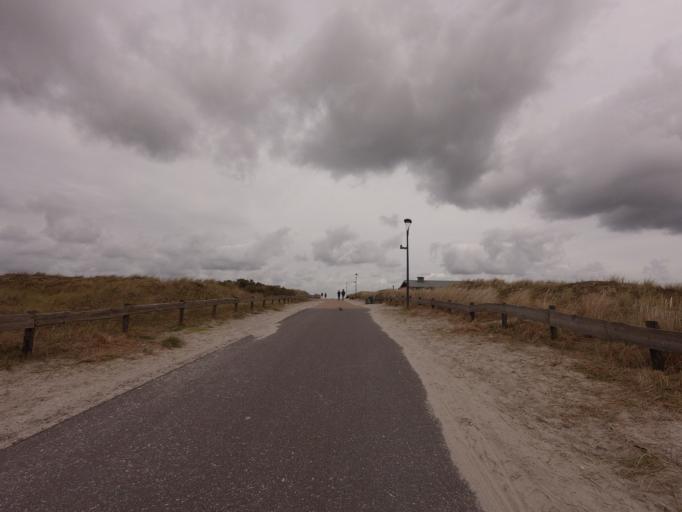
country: NL
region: Friesland
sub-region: Gemeente Ameland
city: Hollum
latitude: 53.4585
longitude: 5.6855
